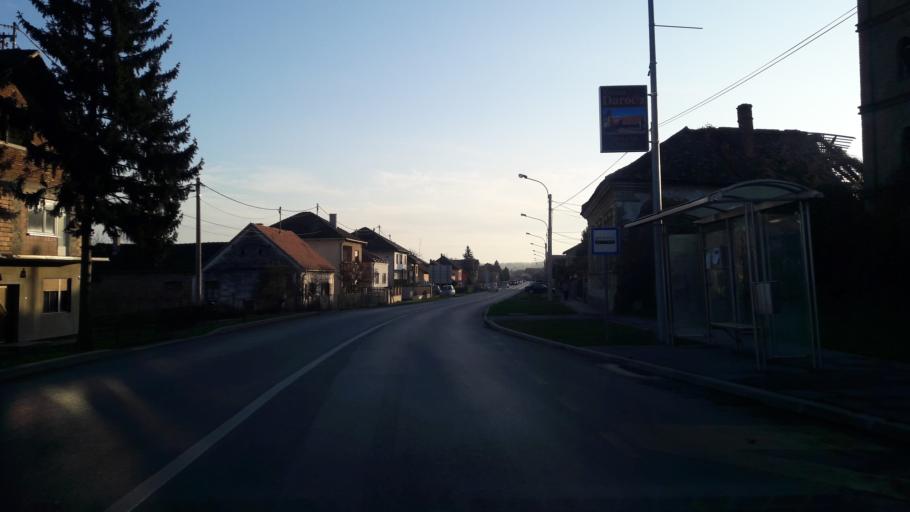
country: HR
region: Osjecko-Baranjska
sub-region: Grad Osijek
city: Bilje
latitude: 45.6026
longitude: 18.7440
